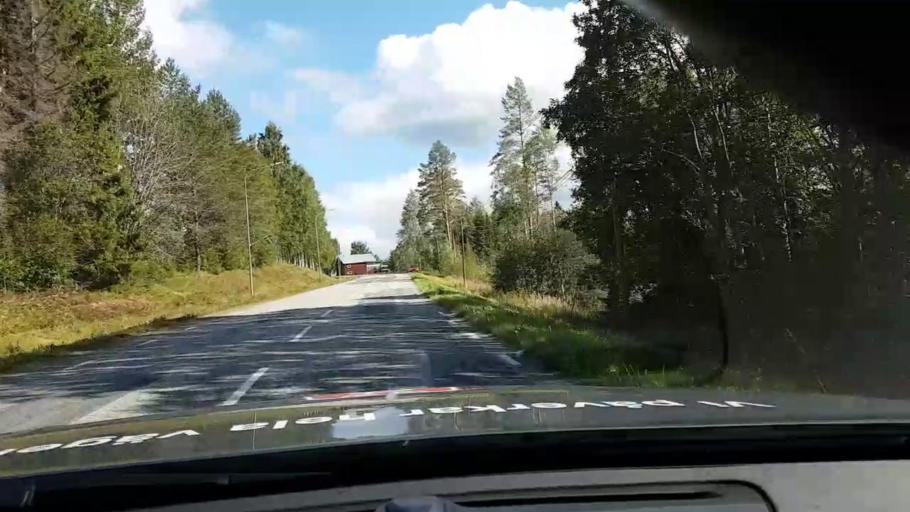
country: SE
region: Vaesterbotten
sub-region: Asele Kommun
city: Asele
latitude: 63.7917
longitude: 17.6216
